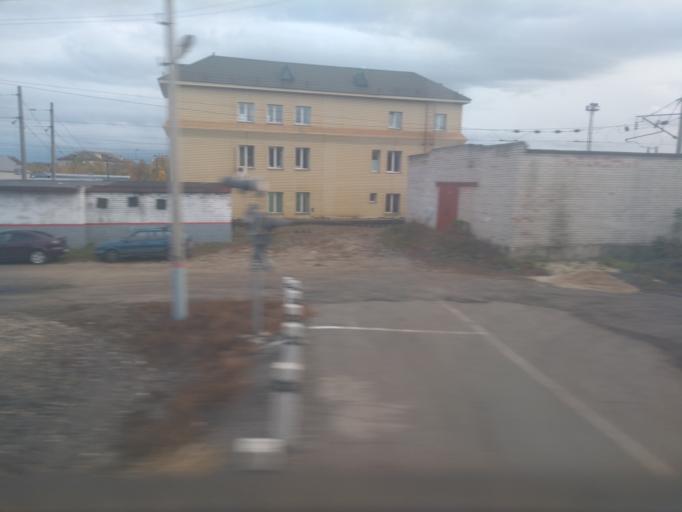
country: RU
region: Tatarstan
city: Staroye Arakchino
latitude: 55.8164
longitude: 48.9051
